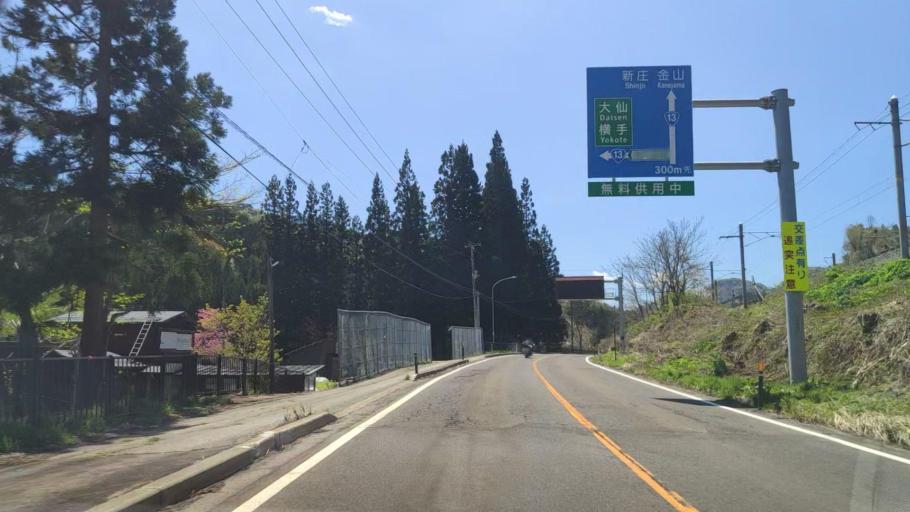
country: JP
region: Akita
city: Yuzawa
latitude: 39.0396
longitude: 140.3929
